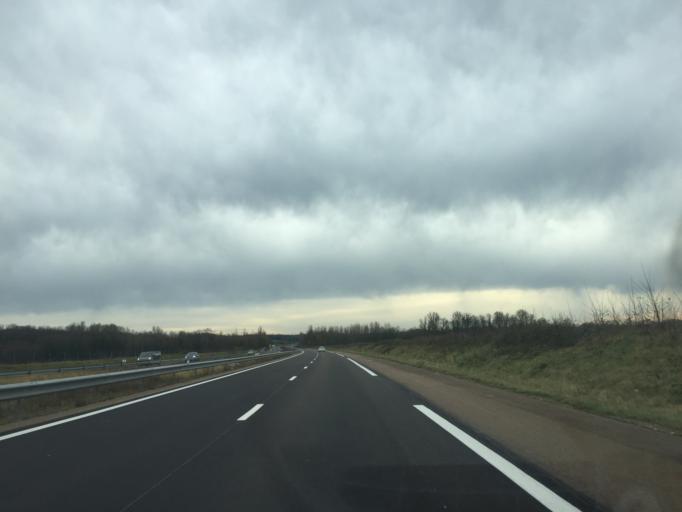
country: FR
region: Franche-Comte
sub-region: Departement du Jura
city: Bletterans
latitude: 46.7538
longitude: 5.5090
